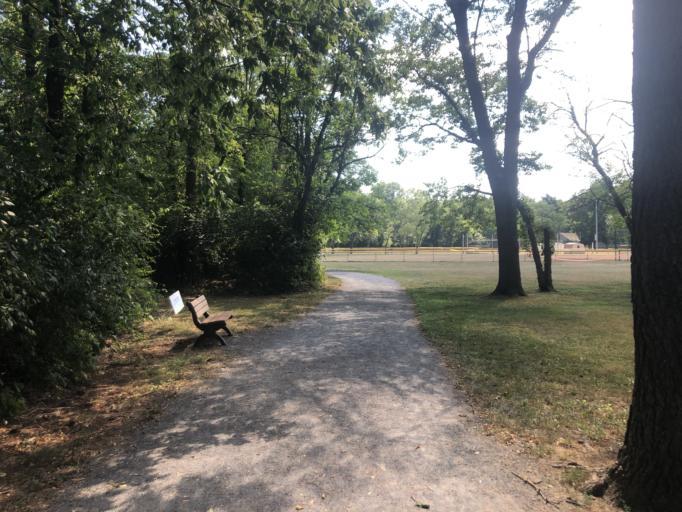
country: US
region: Virginia
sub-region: Clarke County
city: Berryville
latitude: 39.1608
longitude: -78.0022
